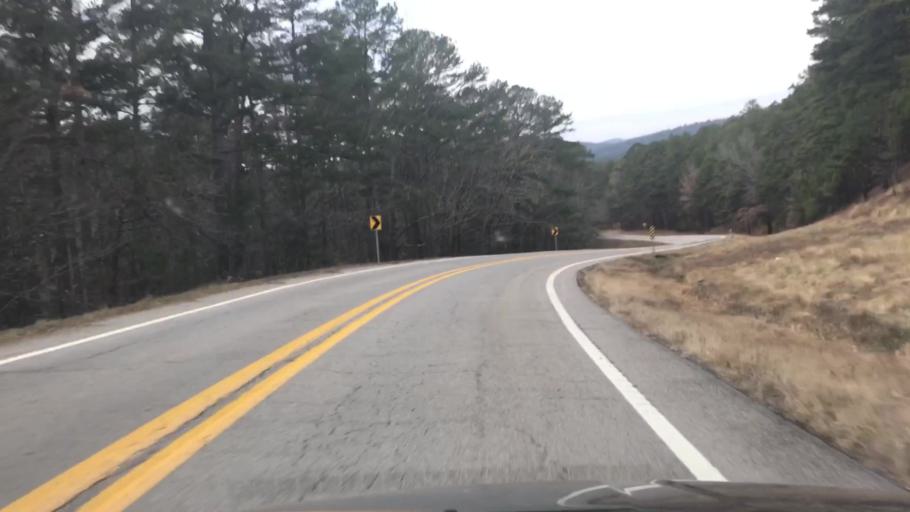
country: US
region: Arkansas
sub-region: Montgomery County
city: Mount Ida
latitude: 34.6838
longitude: -93.8012
